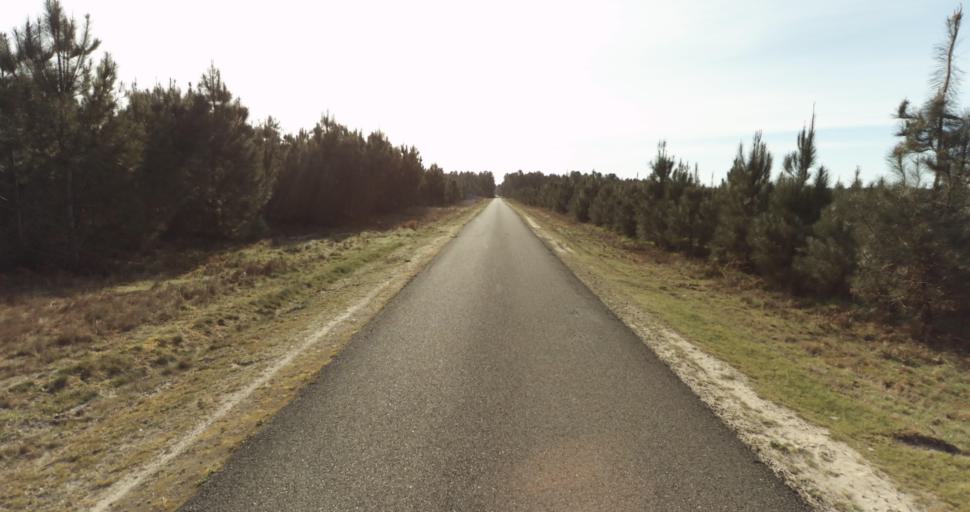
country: FR
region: Aquitaine
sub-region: Departement des Landes
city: Roquefort
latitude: 44.0760
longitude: -0.2712
